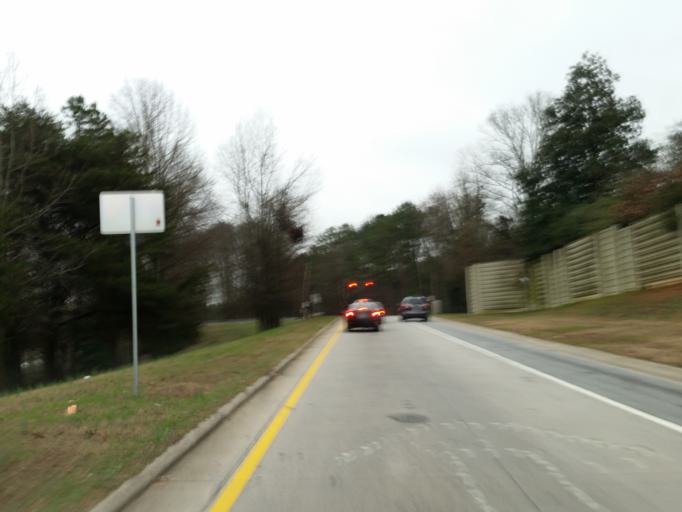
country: US
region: Georgia
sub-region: Fulton County
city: Sandy Springs
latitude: 33.9154
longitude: -84.4079
